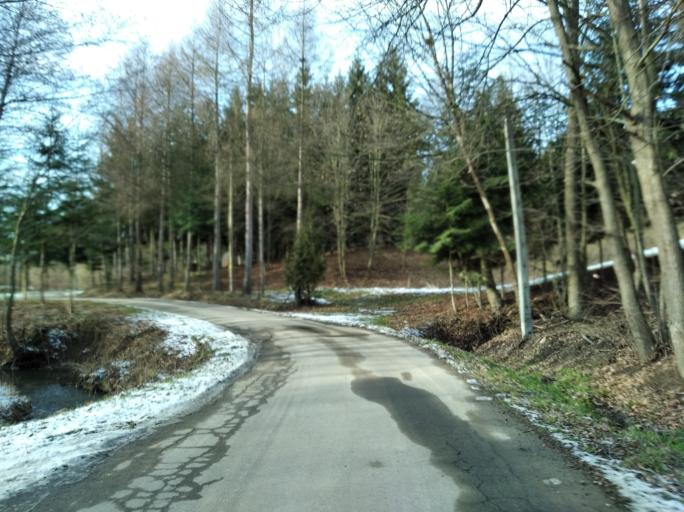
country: PL
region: Subcarpathian Voivodeship
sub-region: Powiat krosnienski
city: Korczyna
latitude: 49.7692
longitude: 21.7964
